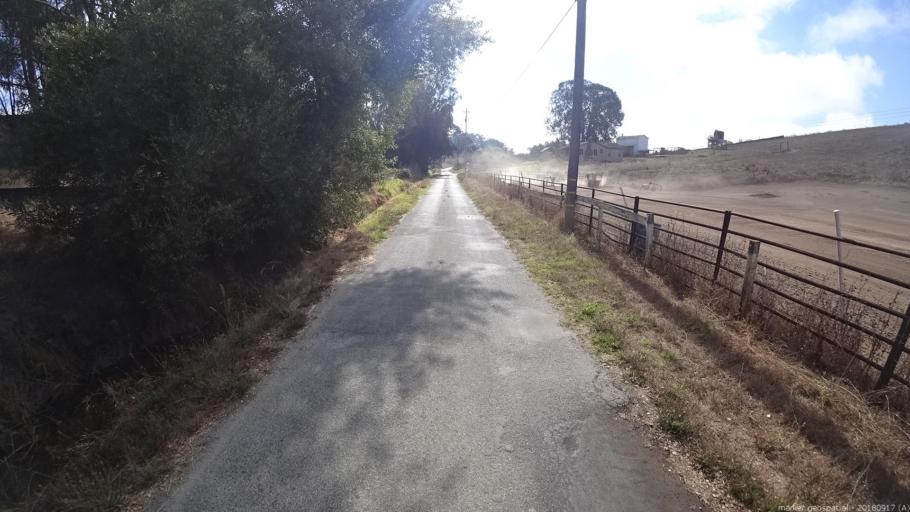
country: US
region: California
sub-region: Monterey County
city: Elkhorn
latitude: 36.7871
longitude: -121.7185
